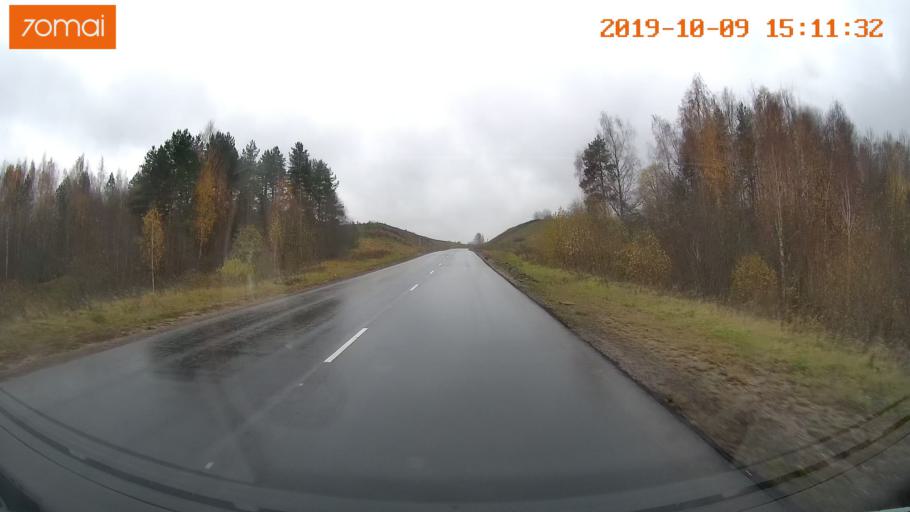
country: RU
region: Kostroma
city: Susanino
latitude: 58.1636
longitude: 41.6294
